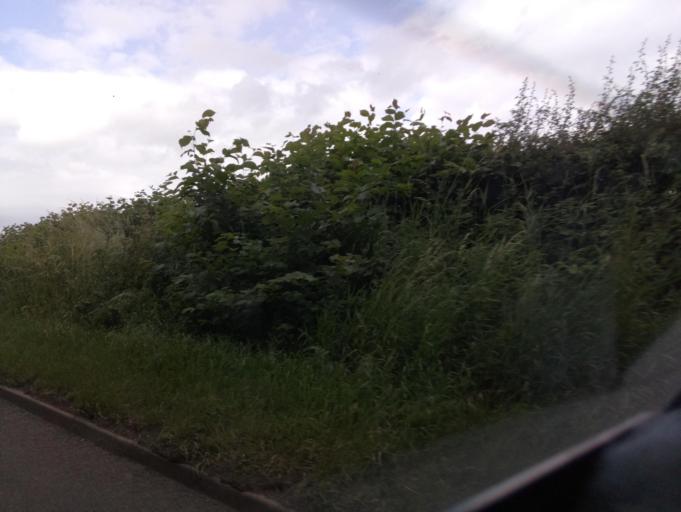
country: GB
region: England
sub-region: Dudley
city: Kingswinford
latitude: 52.4789
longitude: -2.1922
